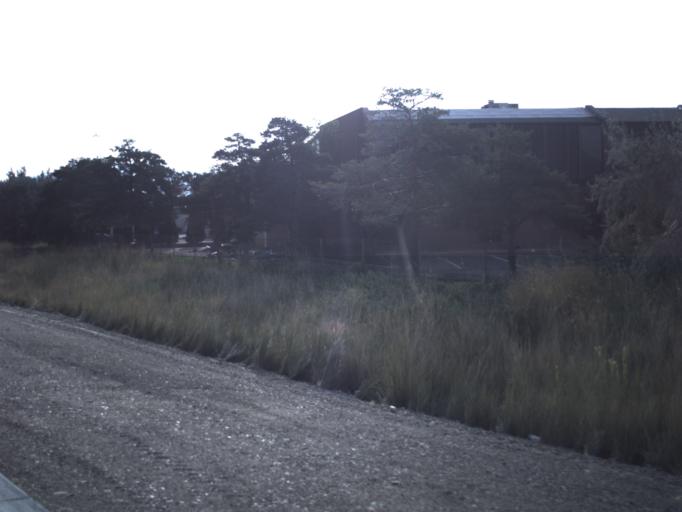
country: US
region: Utah
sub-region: Salt Lake County
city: Taylorsville
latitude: 40.7238
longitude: -111.9485
